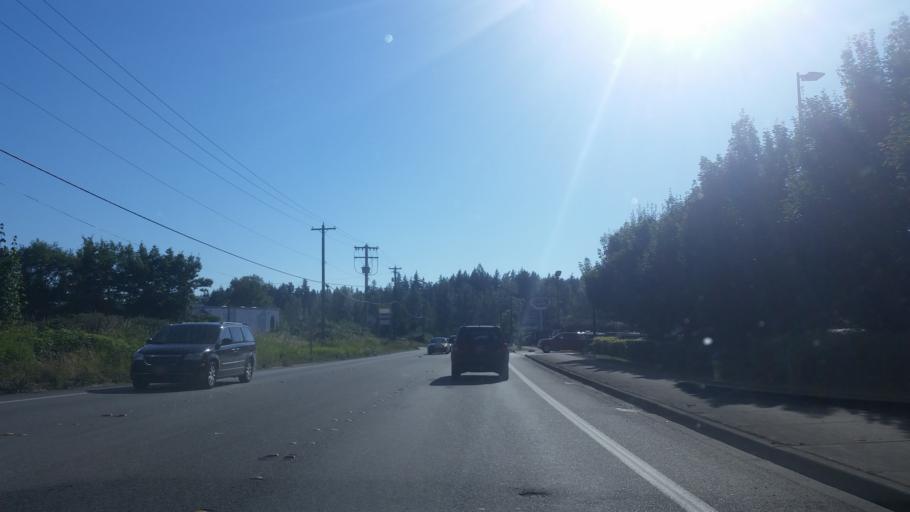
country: US
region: Washington
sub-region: King County
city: Woodinville
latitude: 47.7783
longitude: -122.1487
